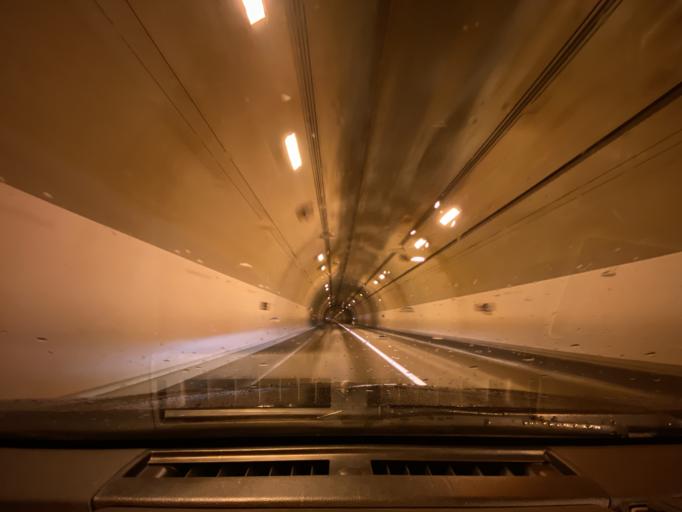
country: JP
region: Hokkaido
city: Rumoi
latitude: 43.6878
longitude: 141.3405
